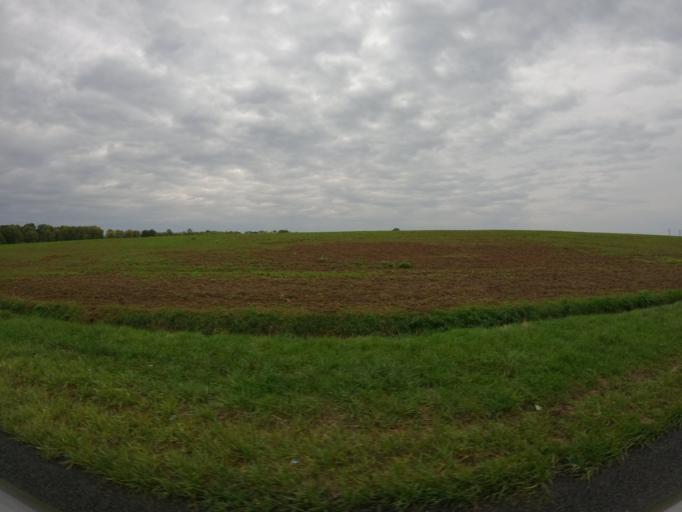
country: FR
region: Ile-de-France
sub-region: Departement de Seine-et-Marne
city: Serris
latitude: 48.8277
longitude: 2.7594
